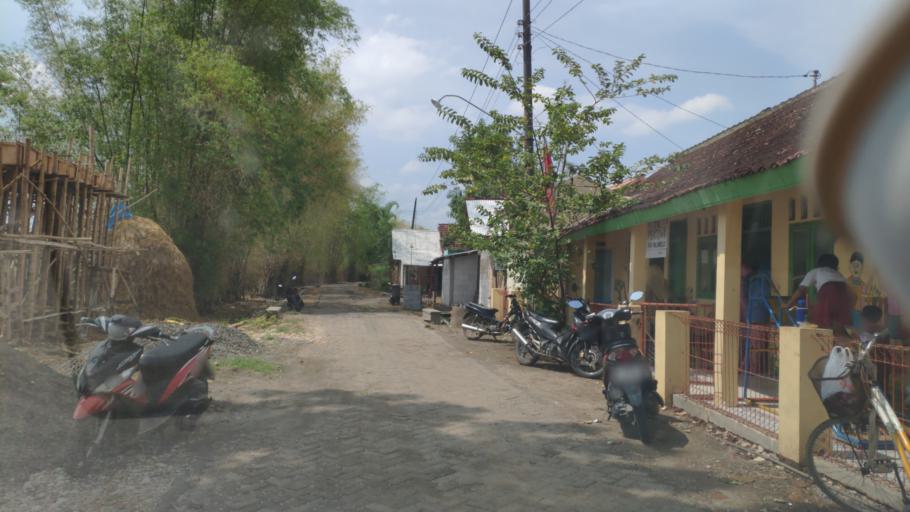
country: ID
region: Central Java
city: Balongrejo
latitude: -7.0098
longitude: 111.3715
